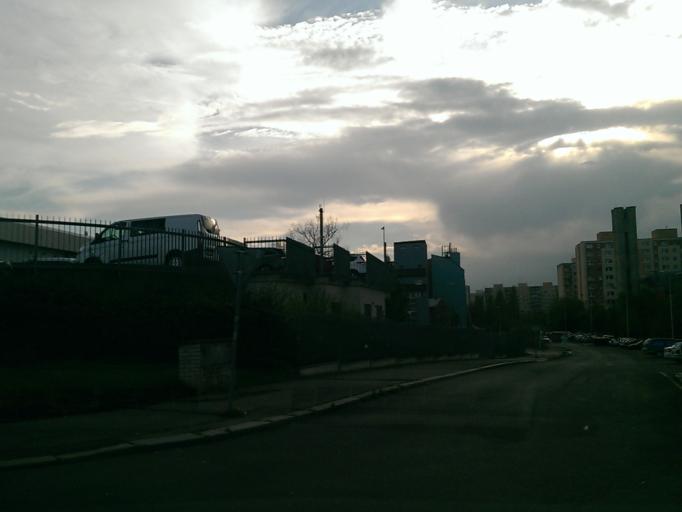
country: CZ
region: Central Bohemia
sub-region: Okres Praha-Zapad
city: Pruhonice
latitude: 50.0369
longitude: 14.5086
